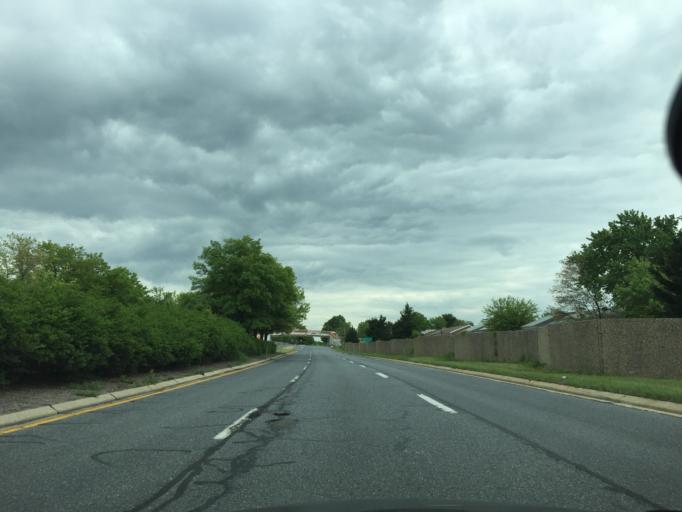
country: US
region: Maryland
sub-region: Baltimore County
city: Essex
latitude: 39.3073
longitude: -76.4499
